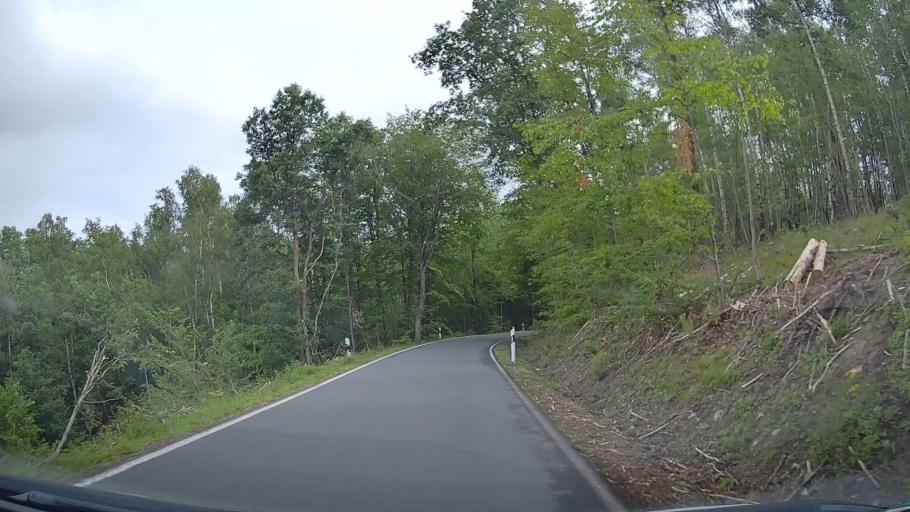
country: DE
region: North Rhine-Westphalia
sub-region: Regierungsbezirk Detmold
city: Barntrup
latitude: 52.0925
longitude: 9.1302
